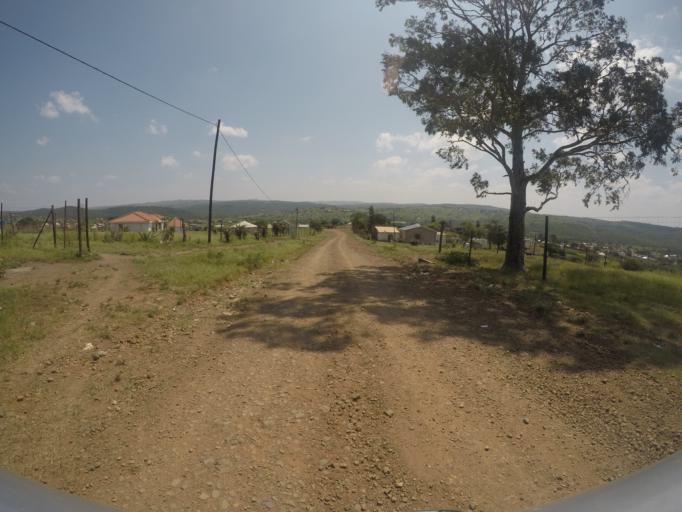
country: ZA
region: KwaZulu-Natal
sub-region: uThungulu District Municipality
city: Empangeni
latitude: -28.5949
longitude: 31.7408
